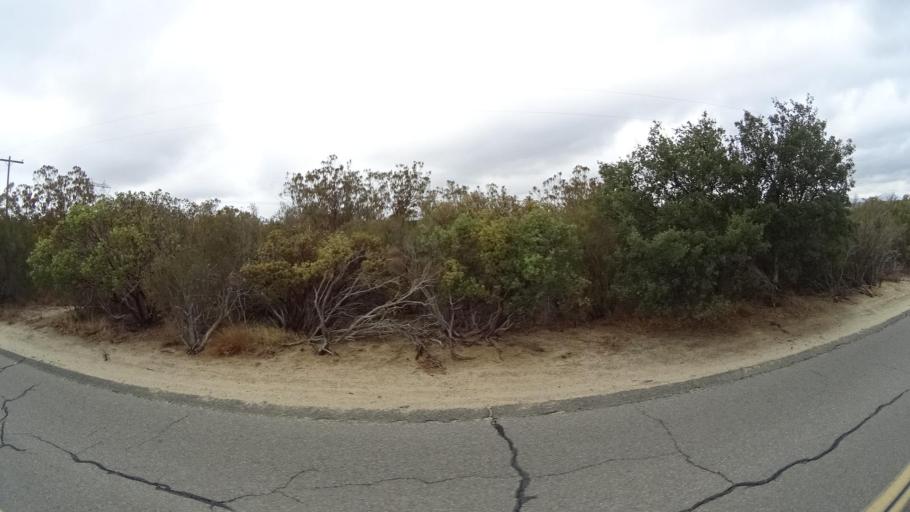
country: US
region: California
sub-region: San Diego County
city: Campo
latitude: 32.6055
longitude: -116.3371
